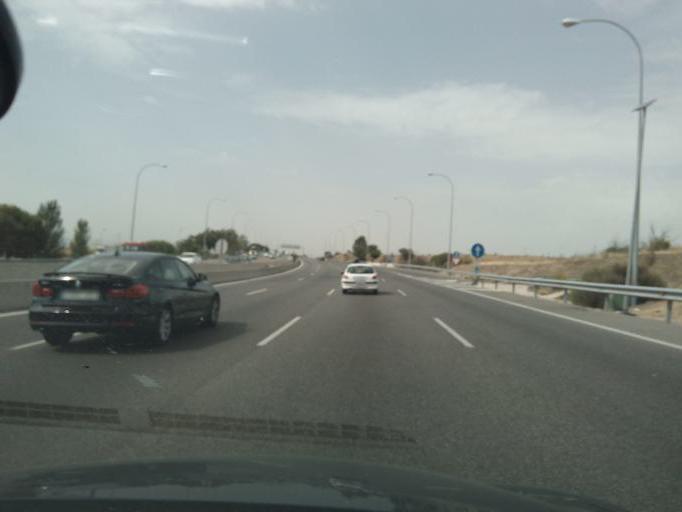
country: ES
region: Madrid
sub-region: Provincia de Madrid
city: Fuencarral-El Pardo
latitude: 40.5017
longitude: -3.7204
